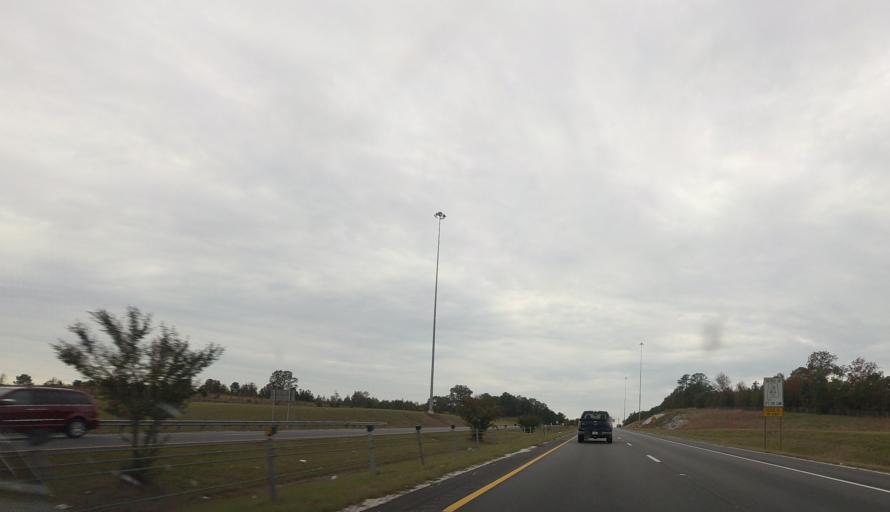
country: US
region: Alabama
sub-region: Russell County
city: Phenix City
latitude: 32.5049
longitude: -85.0056
